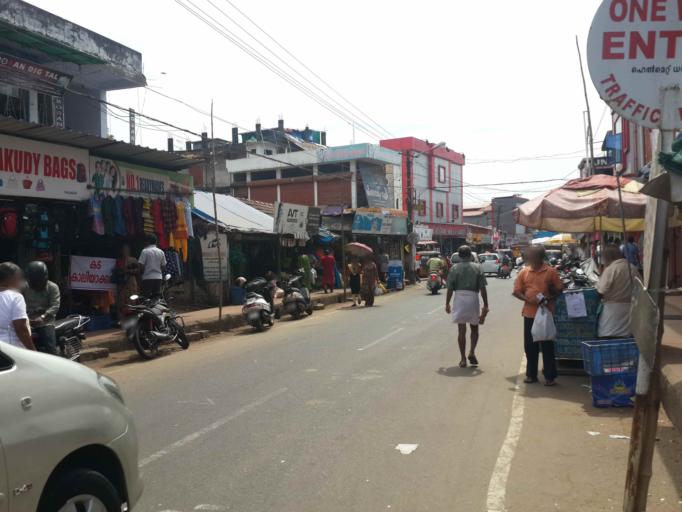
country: IN
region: Kerala
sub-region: Thrissur District
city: Kizhake Chalakudi
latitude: 10.3077
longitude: 76.3385
